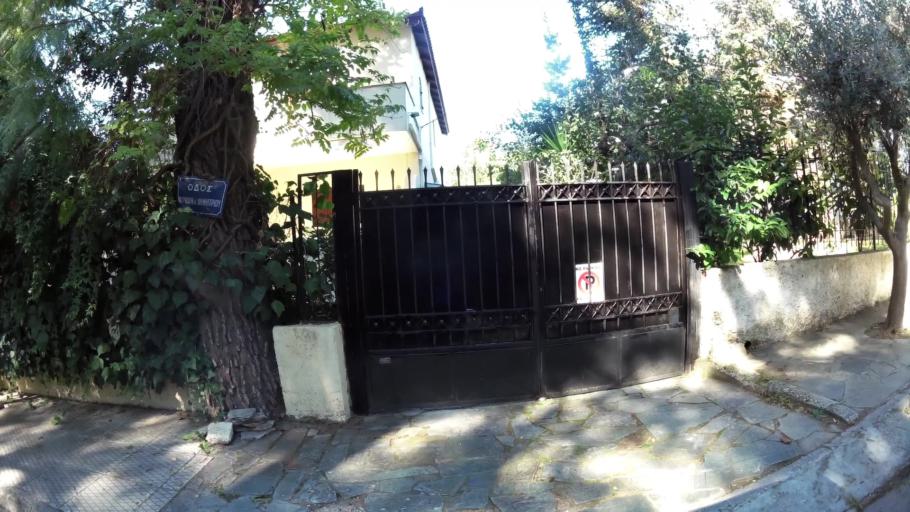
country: GR
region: Attica
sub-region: Nomarchia Anatolikis Attikis
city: Drosia
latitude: 38.1192
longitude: 23.8598
